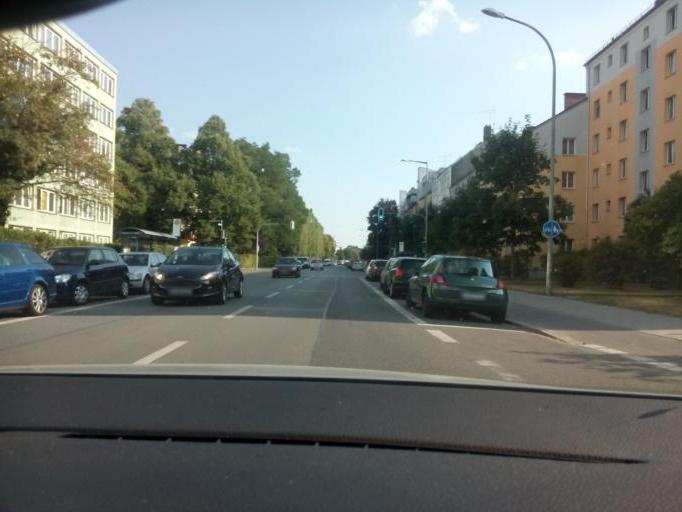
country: DE
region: Bavaria
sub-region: Upper Bavaria
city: Munich
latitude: 48.1144
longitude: 11.6034
